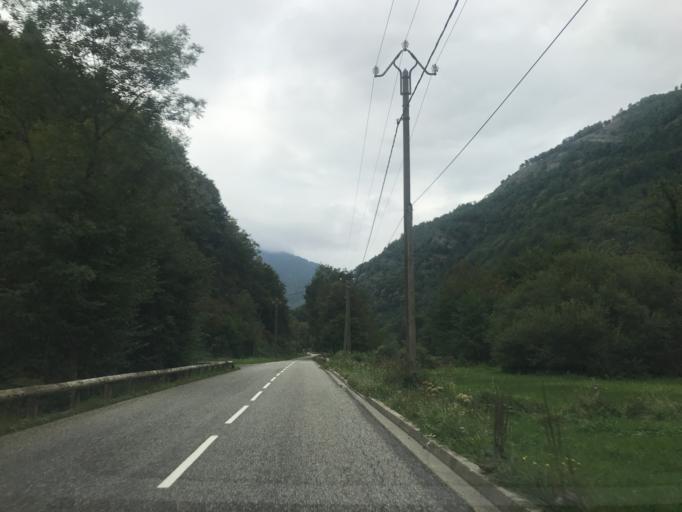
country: FR
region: Midi-Pyrenees
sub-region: Departement de la Haute-Garonne
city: Bagneres-de-Luchon
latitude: 42.7697
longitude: 0.6307
